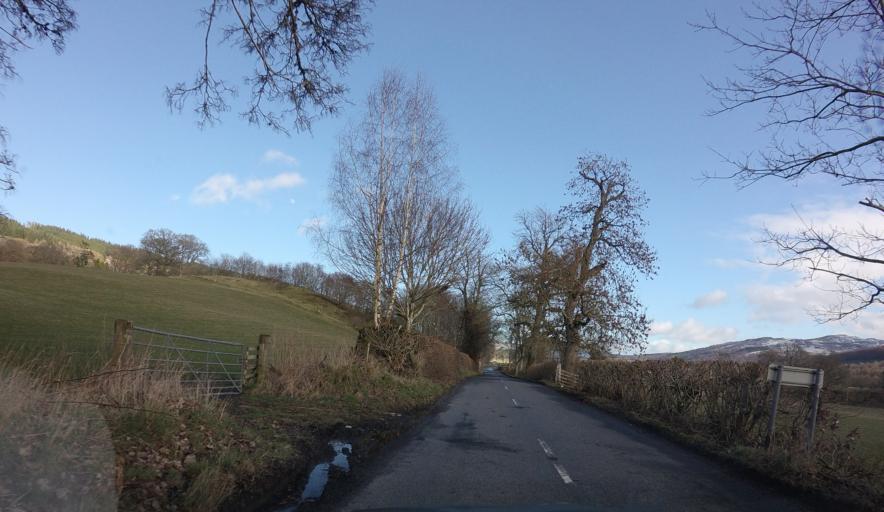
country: GB
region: Scotland
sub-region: Perth and Kinross
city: Pitlochry
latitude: 56.6608
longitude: -3.7540
